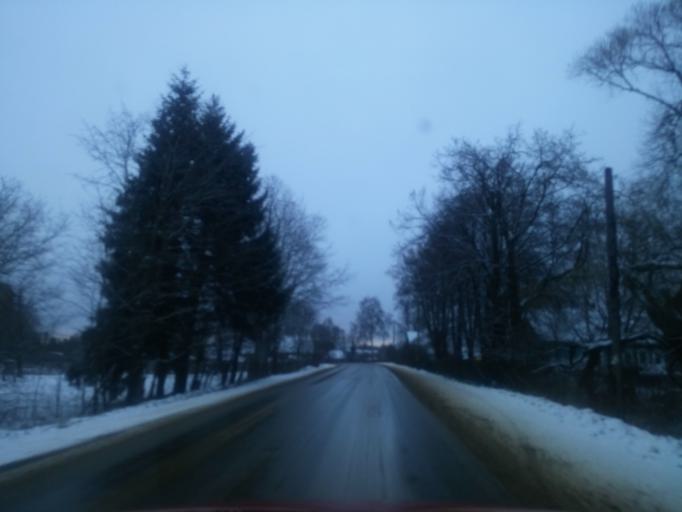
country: RU
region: Tverskaya
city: Likhoslavl'
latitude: 56.9885
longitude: 35.4418
